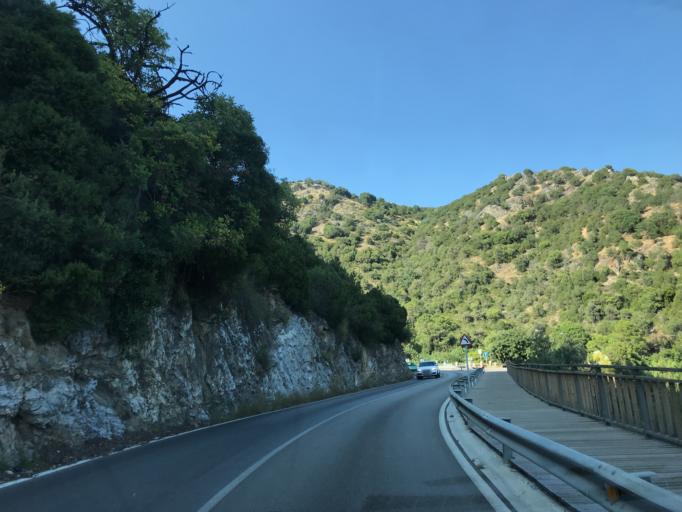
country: ES
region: Andalusia
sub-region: Provincia de Malaga
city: Benahavis
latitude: 36.5123
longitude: -5.0353
